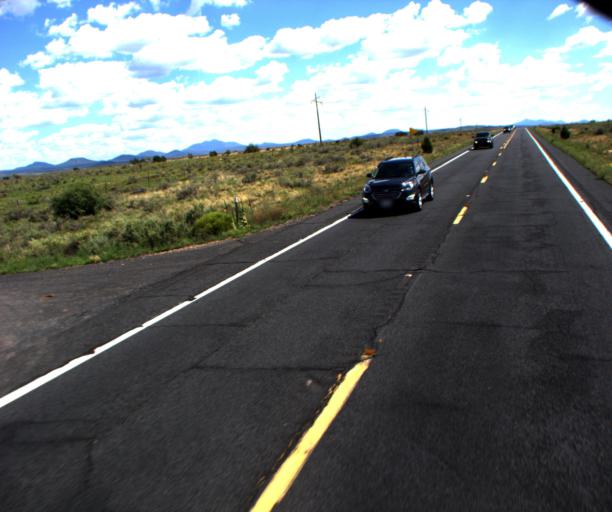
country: US
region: Arizona
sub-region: Coconino County
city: Williams
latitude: 35.6283
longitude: -112.1427
